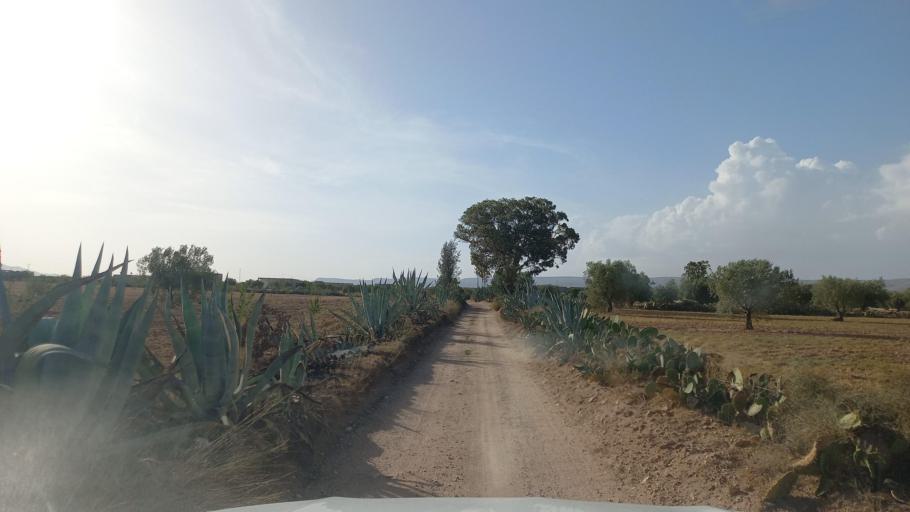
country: TN
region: Al Qasrayn
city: Kasserine
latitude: 35.2280
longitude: 8.9302
